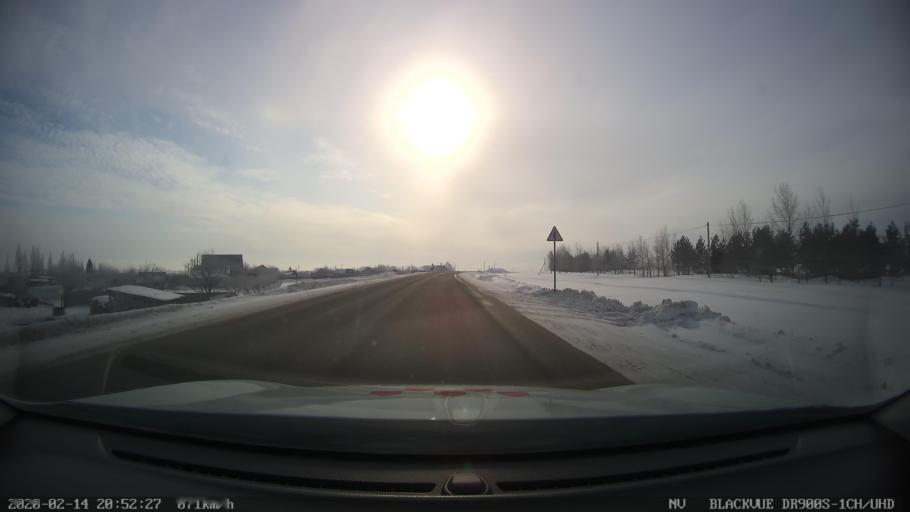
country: RU
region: Tatarstan
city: Kuybyshevskiy Zaton
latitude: 55.2042
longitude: 49.2491
